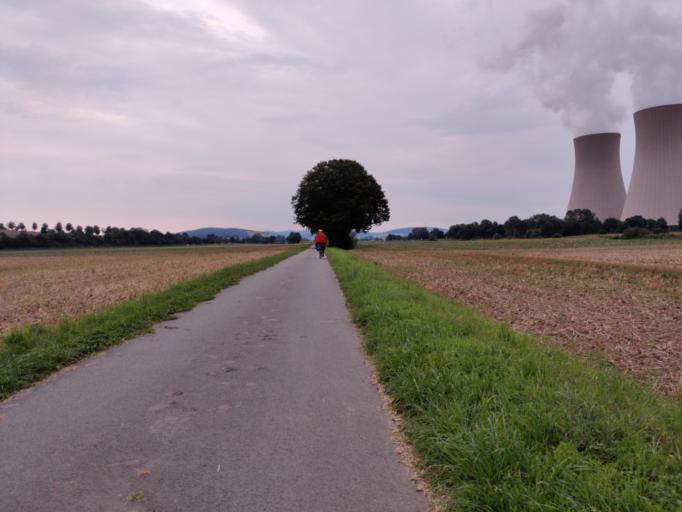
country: DE
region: Lower Saxony
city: Hehlen
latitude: 52.0433
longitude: 9.4126
